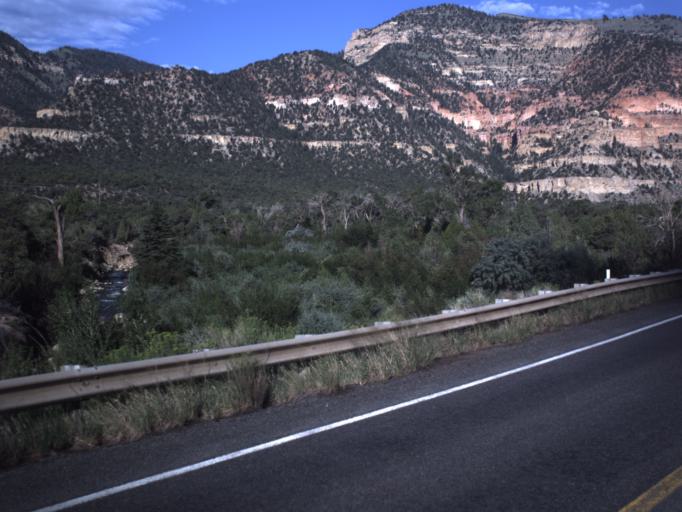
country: US
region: Utah
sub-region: Emery County
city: Huntington
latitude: 39.3922
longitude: -111.0937
